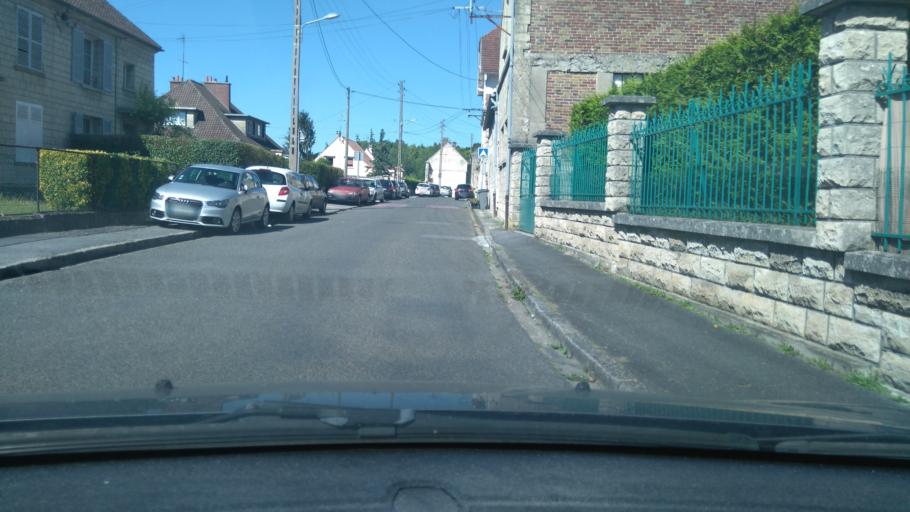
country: FR
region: Picardie
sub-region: Departement de l'Oise
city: Saint-Maximin
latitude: 49.2241
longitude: 2.4414
